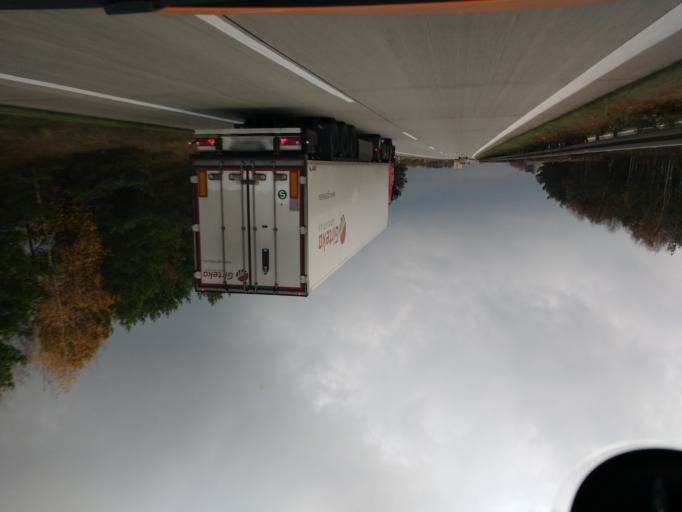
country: DE
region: Brandenburg
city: Heiligengrabe
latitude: 53.1645
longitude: 12.3788
